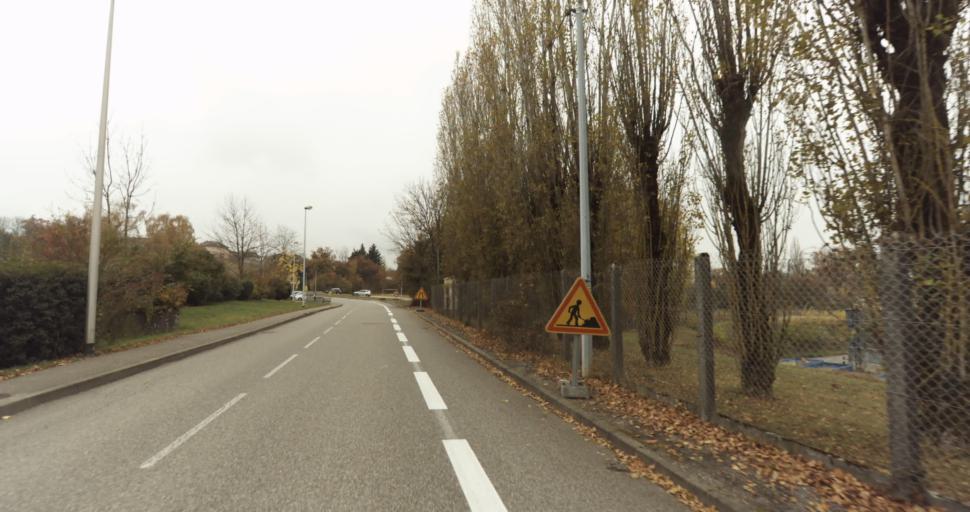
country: FR
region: Rhone-Alpes
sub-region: Departement de la Haute-Savoie
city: Seynod
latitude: 45.8868
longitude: 6.0886
